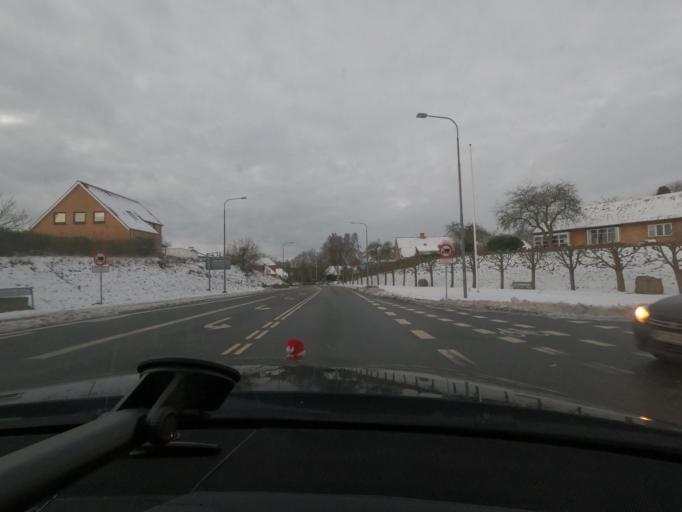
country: DK
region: South Denmark
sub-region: Sonderborg Kommune
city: Grasten
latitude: 54.9269
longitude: 9.5993
